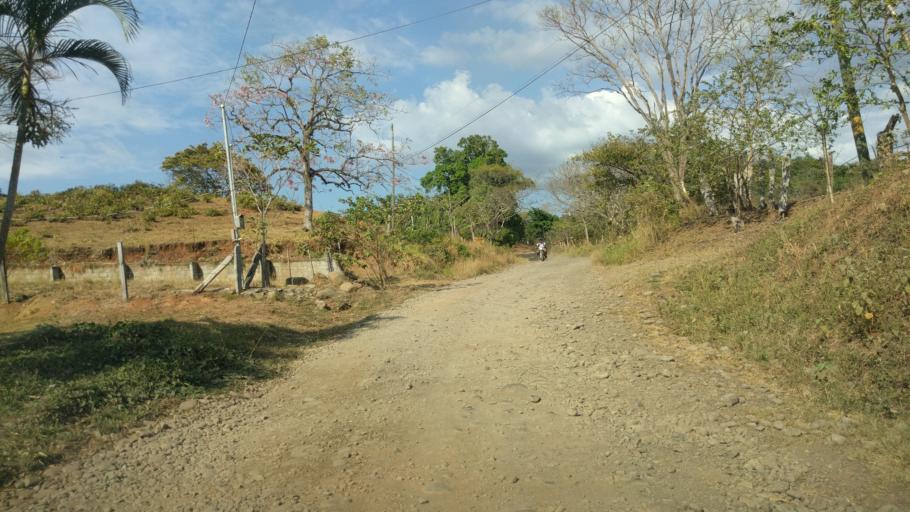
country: CR
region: Puntarenas
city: Esparza
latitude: 10.0156
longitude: -84.6906
